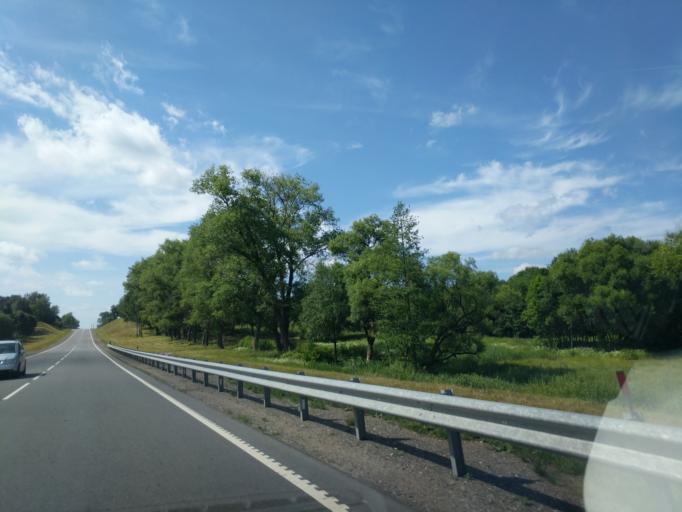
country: BY
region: Minsk
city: Syomkava
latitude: 54.1052
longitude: 27.4697
